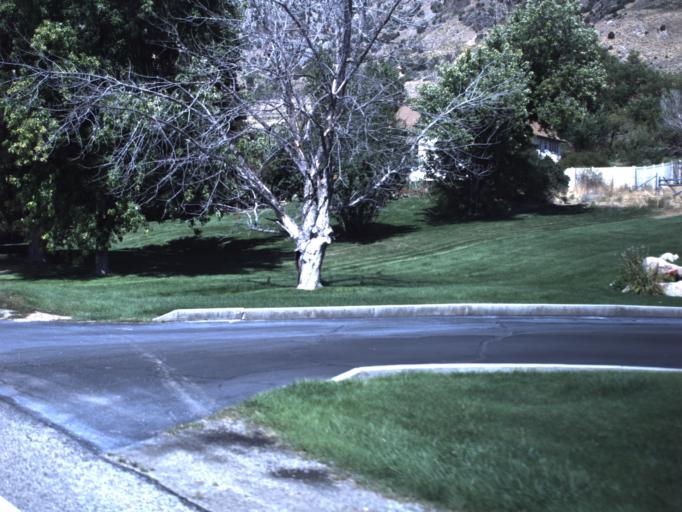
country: US
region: Utah
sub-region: Box Elder County
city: Honeyville
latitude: 41.5964
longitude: -112.0463
